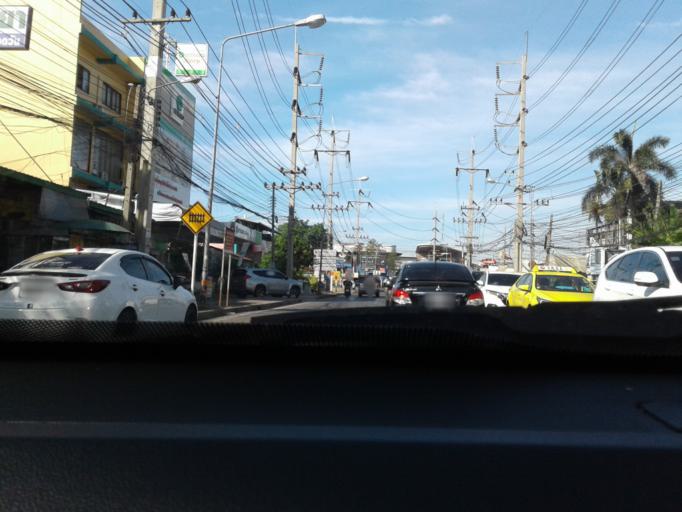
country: TH
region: Nakhon Pathom
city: Salaya
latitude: 13.8018
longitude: 100.3203
